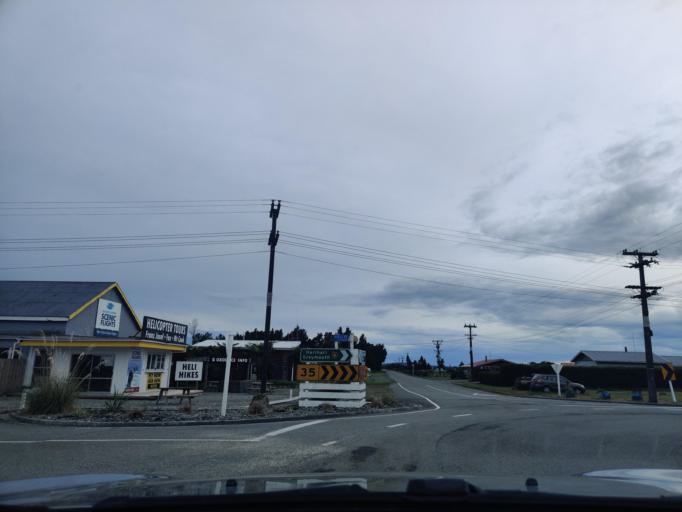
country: NZ
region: West Coast
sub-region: Westland District
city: Hokitika
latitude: -43.2617
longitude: 170.3589
